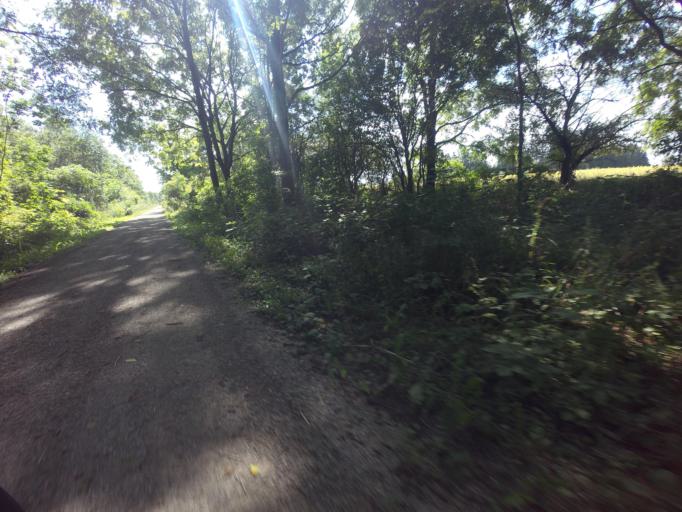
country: CA
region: Ontario
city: Huron East
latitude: 43.6913
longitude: -81.3263
